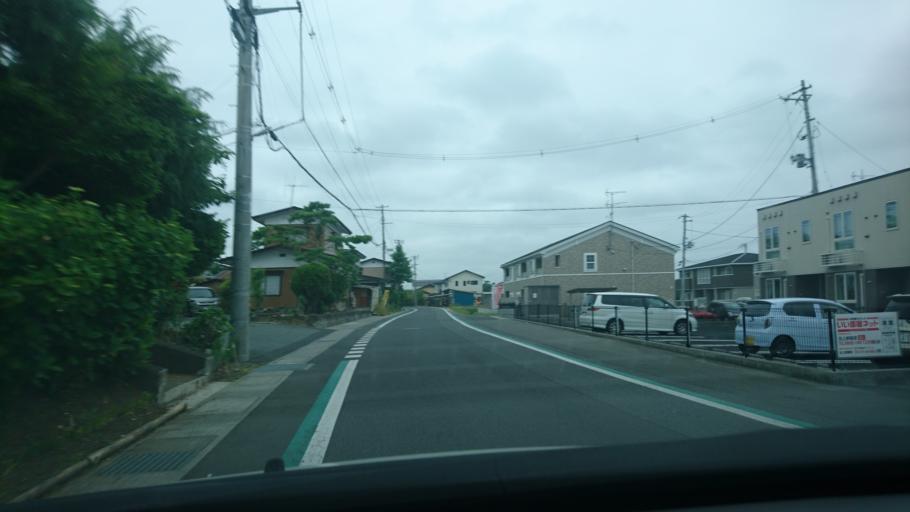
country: JP
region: Iwate
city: Ichinoseki
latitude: 38.9133
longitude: 141.1027
